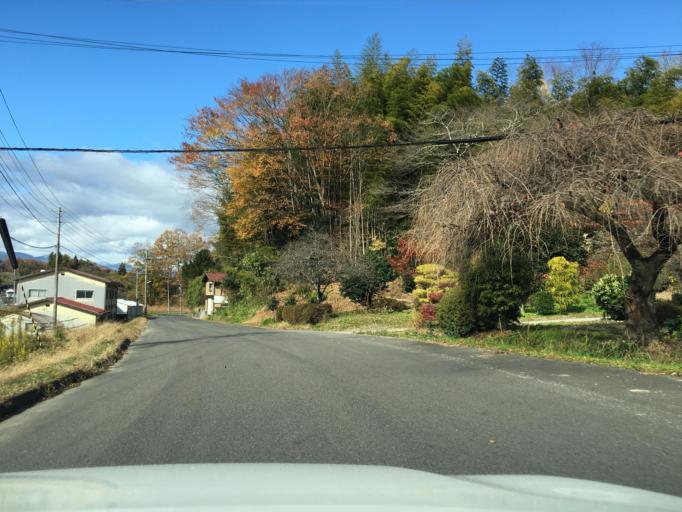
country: JP
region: Fukushima
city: Miharu
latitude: 37.5047
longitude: 140.4952
